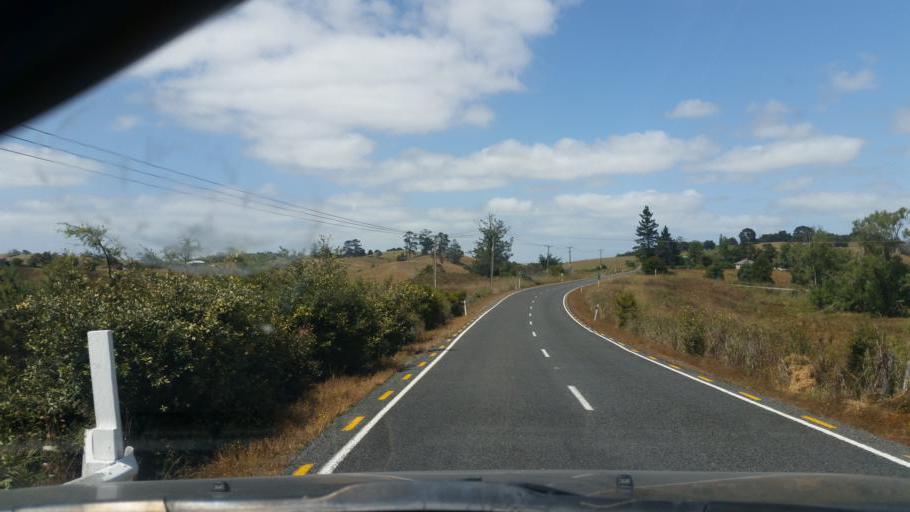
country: NZ
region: Northland
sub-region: Whangarei
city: Ruakaka
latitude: -36.0381
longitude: 174.2795
